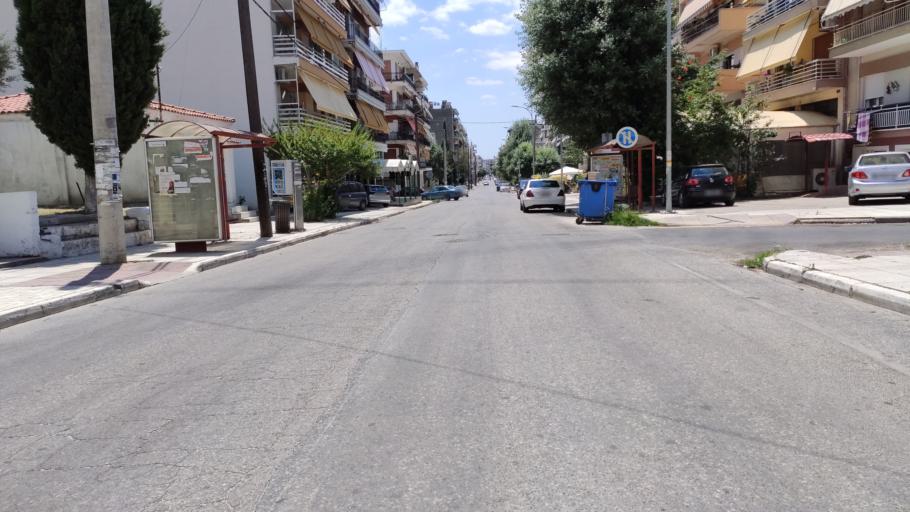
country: GR
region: East Macedonia and Thrace
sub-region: Nomos Rodopis
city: Komotini
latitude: 41.1275
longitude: 25.4119
